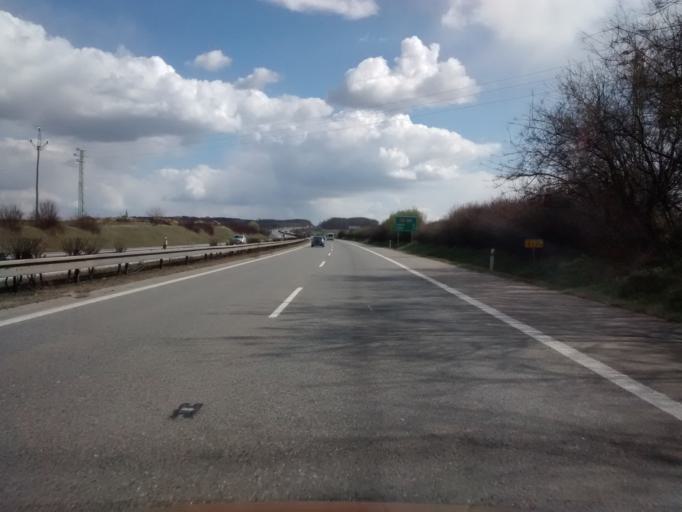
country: CZ
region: Central Bohemia
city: Odolena Voda
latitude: 50.2421
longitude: 14.3803
